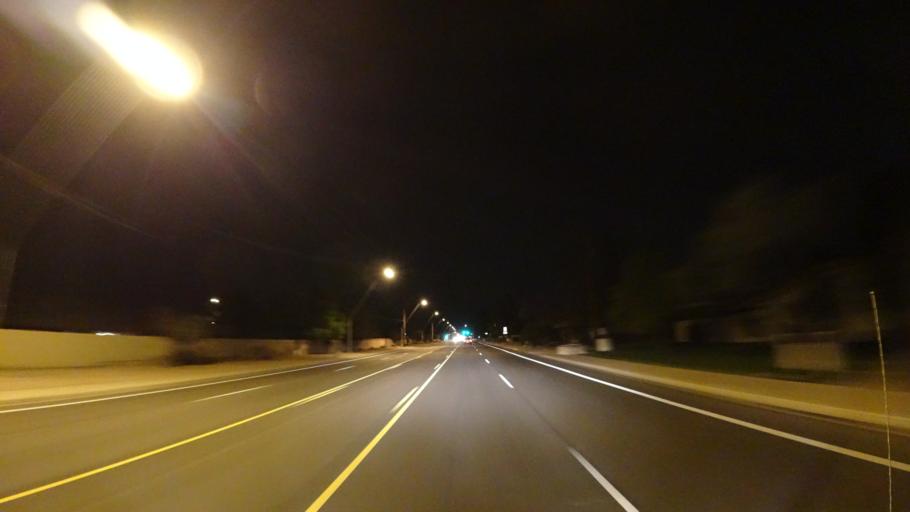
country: US
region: Arizona
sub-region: Maricopa County
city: Mesa
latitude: 33.4370
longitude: -111.8000
